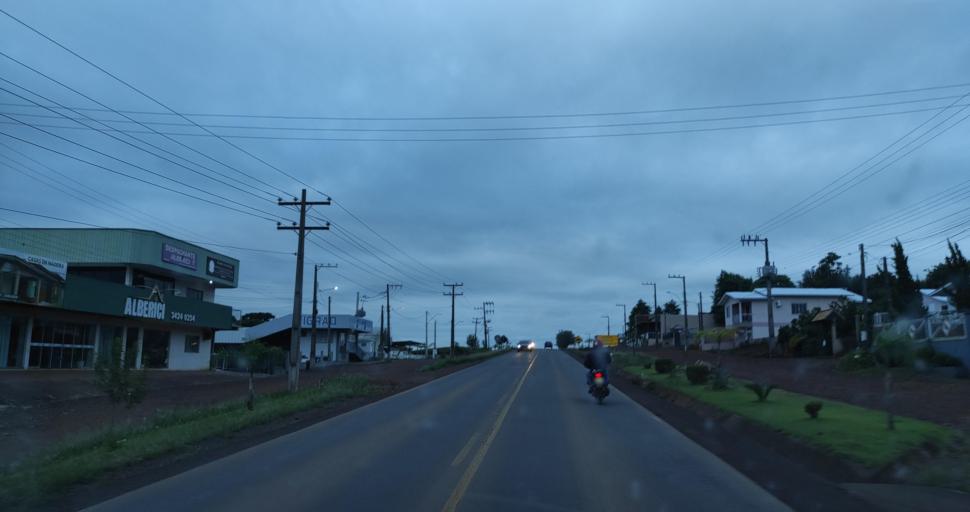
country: BR
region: Santa Catarina
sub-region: Xanxere
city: Xanxere
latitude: -26.7392
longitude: -52.3942
